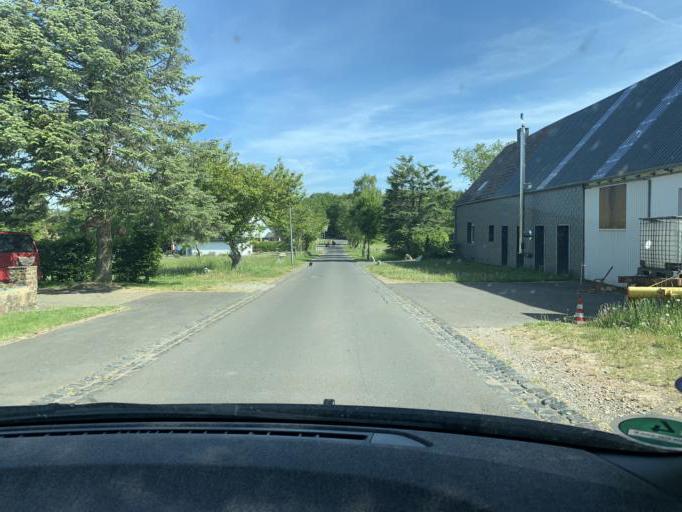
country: DE
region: North Rhine-Westphalia
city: Heimbach
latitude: 50.5913
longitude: 6.4961
